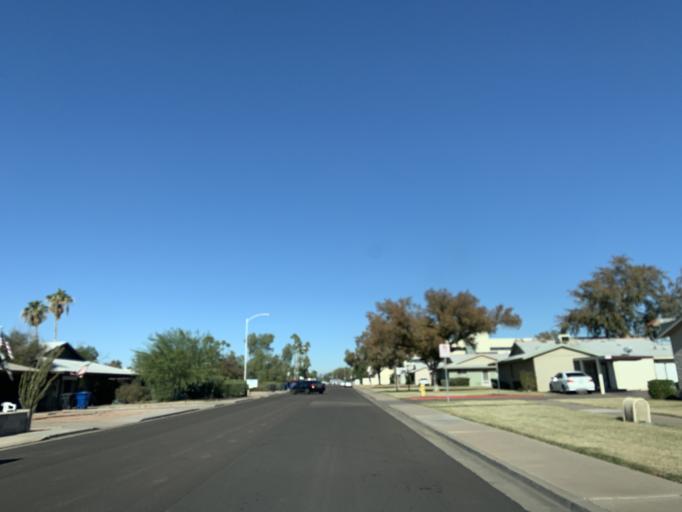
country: US
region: Arizona
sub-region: Maricopa County
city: Mesa
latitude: 33.4189
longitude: -111.8609
